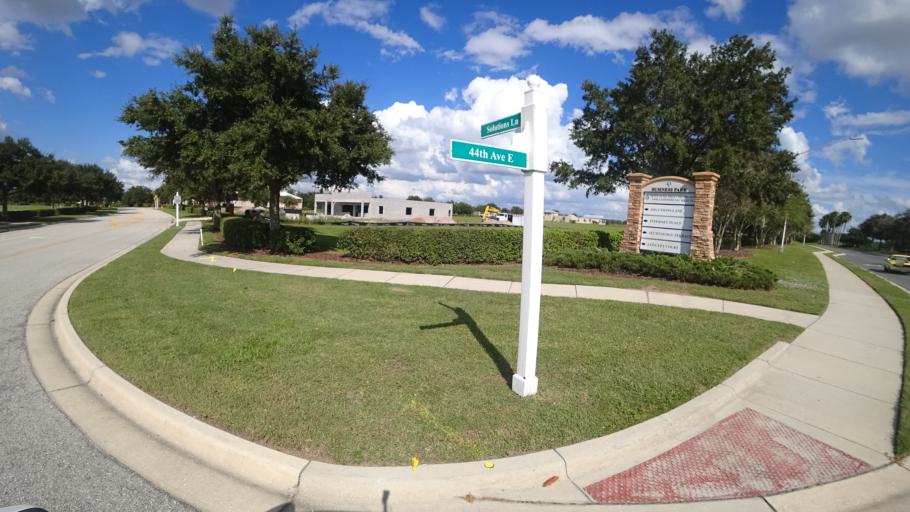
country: US
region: Florida
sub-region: Sarasota County
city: Desoto Lakes
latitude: 27.4589
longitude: -82.4369
